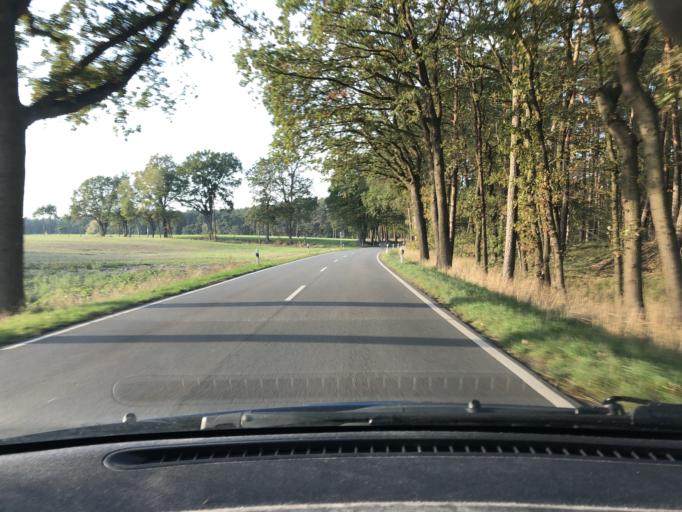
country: DE
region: Lower Saxony
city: Hitzacker
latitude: 53.1209
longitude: 11.0514
